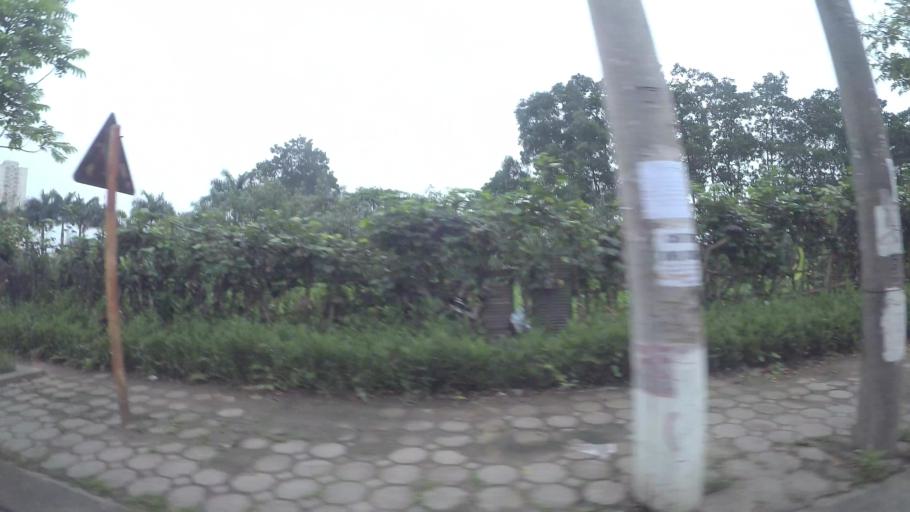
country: VN
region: Ha Noi
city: Hai BaTrung
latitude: 20.9942
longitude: 105.8835
